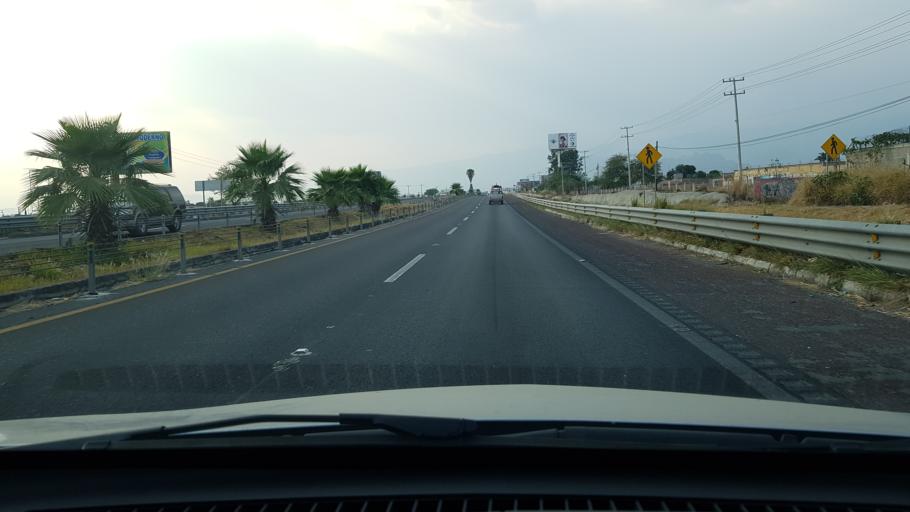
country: MX
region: Morelos
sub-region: Cuautla
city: Tierra Larga (Campo Nuevo)
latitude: 18.8585
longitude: -98.9437
